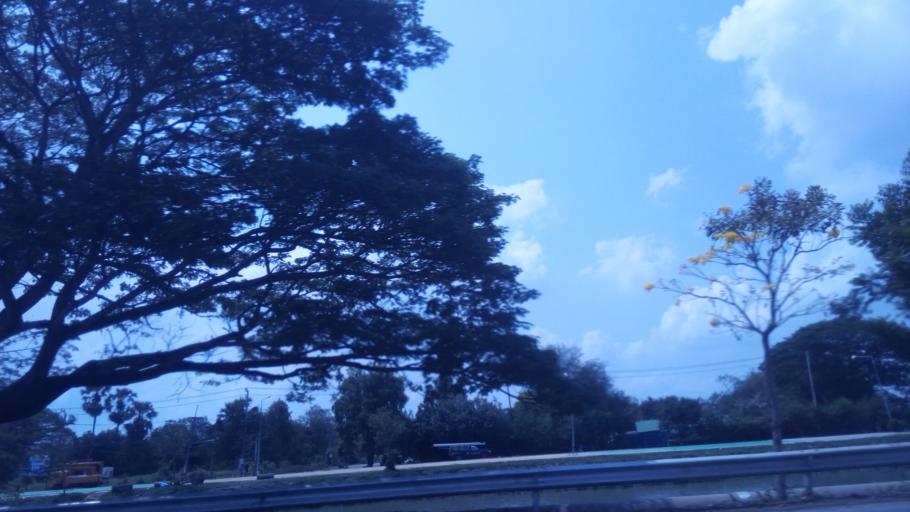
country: TH
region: Pathum Thani
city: Ban Rangsit
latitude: 14.0490
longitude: 100.8116
